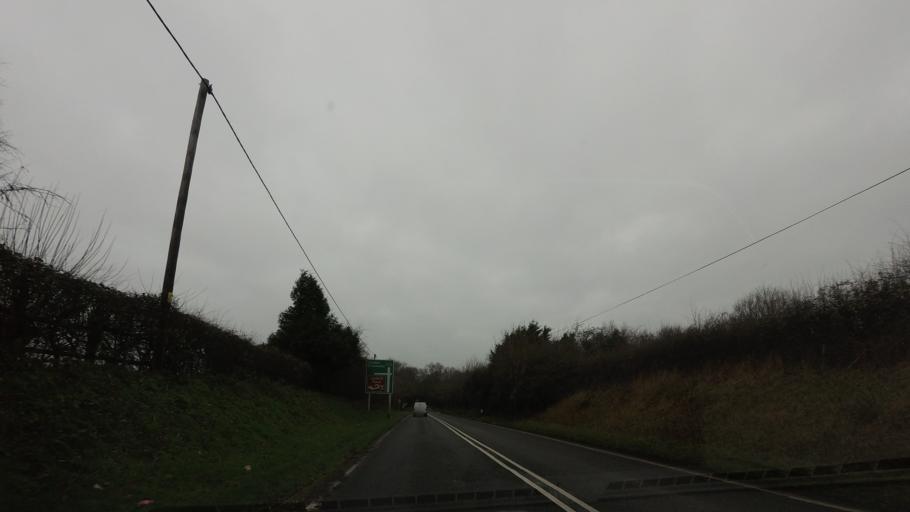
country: GB
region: England
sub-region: East Sussex
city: Battle
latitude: 50.9407
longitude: 0.5140
